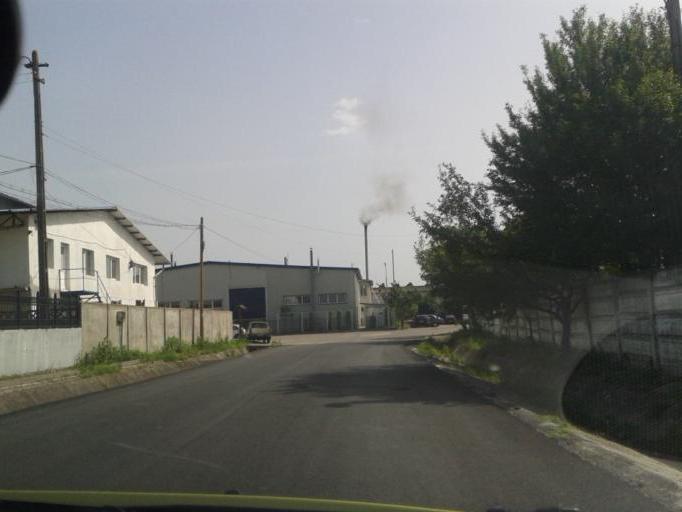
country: RO
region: Valcea
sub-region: Oras Ocnele Mari
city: Ocnele Mari
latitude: 45.0692
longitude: 24.3387
